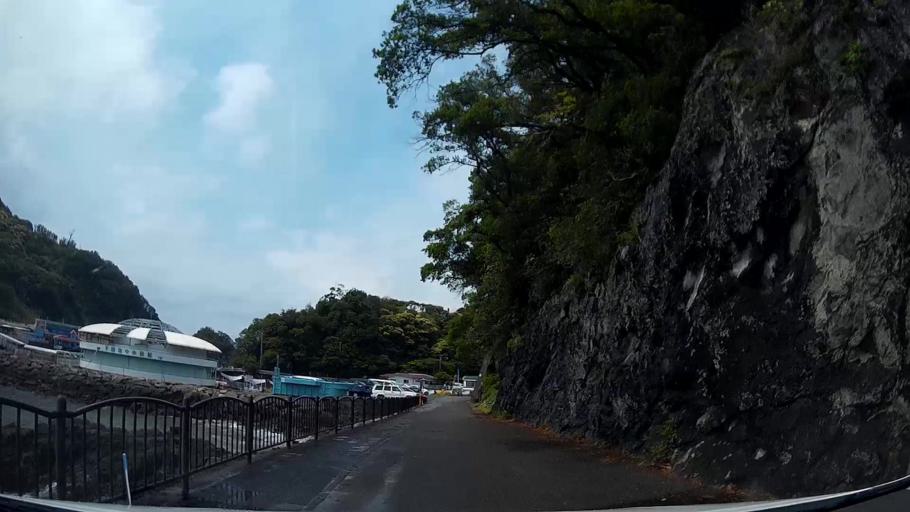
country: JP
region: Shizuoka
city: Shimoda
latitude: 34.6662
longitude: 138.9477
